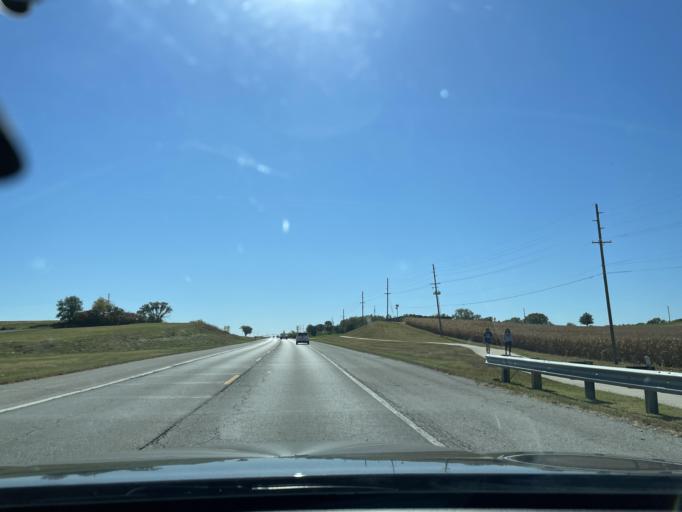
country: US
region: Missouri
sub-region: Buchanan County
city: Saint Joseph
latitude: 39.7648
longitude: -94.7688
